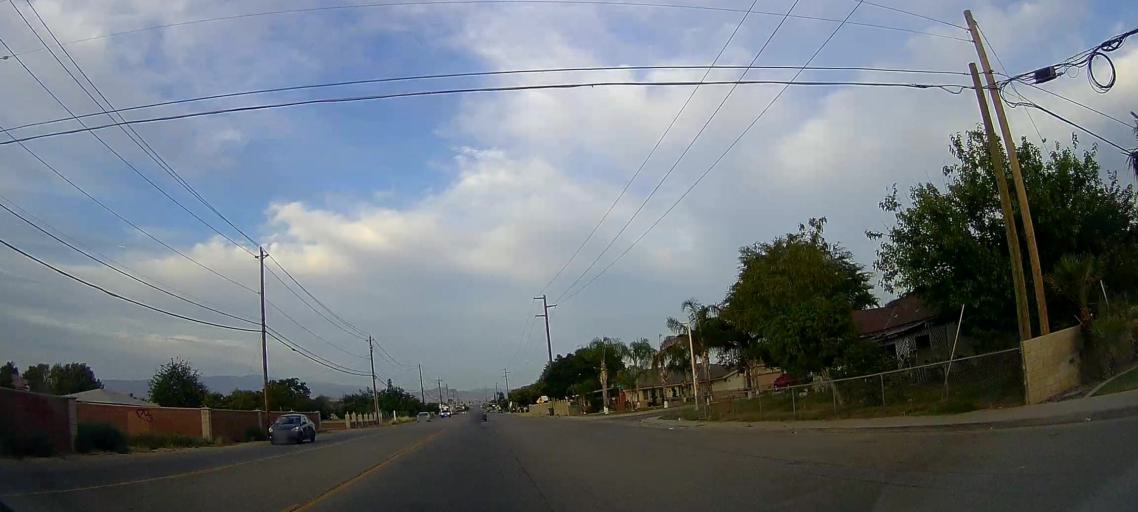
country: US
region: California
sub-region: Kern County
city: Bakersfield
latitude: 35.3542
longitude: -118.9364
